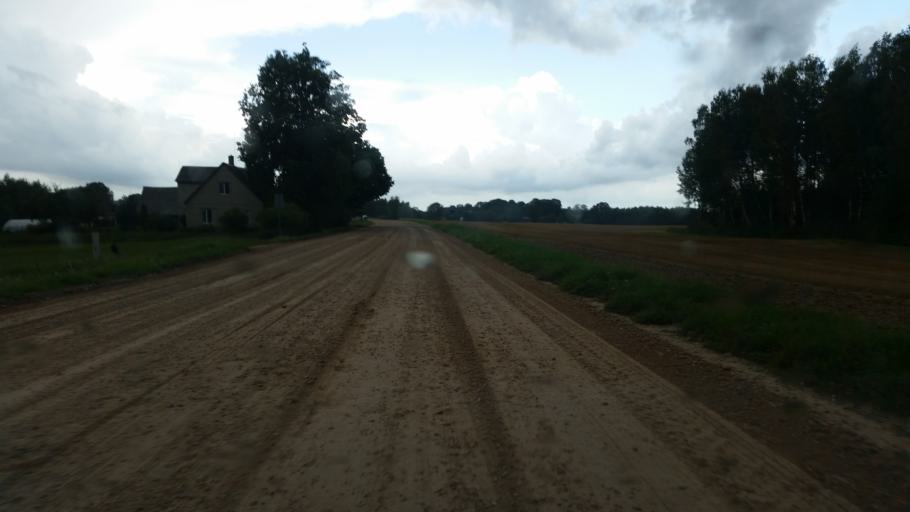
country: LV
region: Vecumnieki
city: Vecumnieki
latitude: 56.4242
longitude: 24.4946
